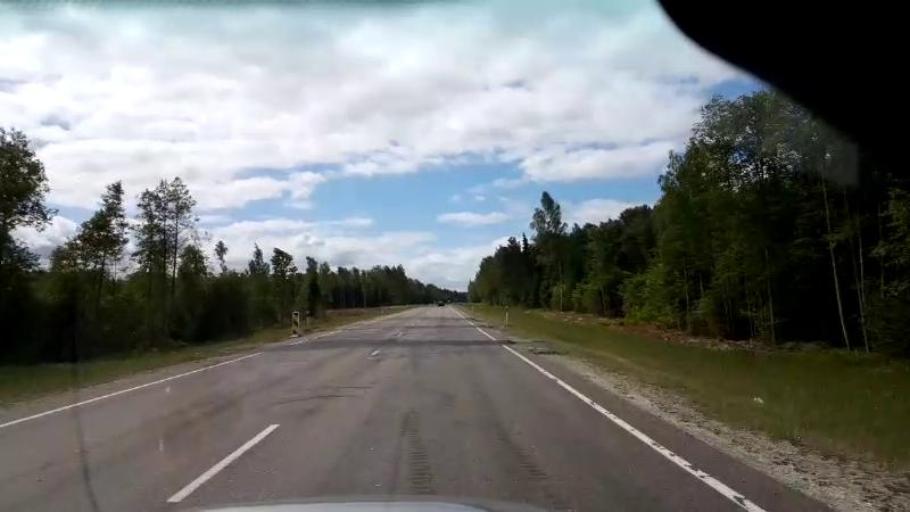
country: LV
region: Salacgrivas
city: Ainazi
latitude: 58.0323
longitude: 24.5052
